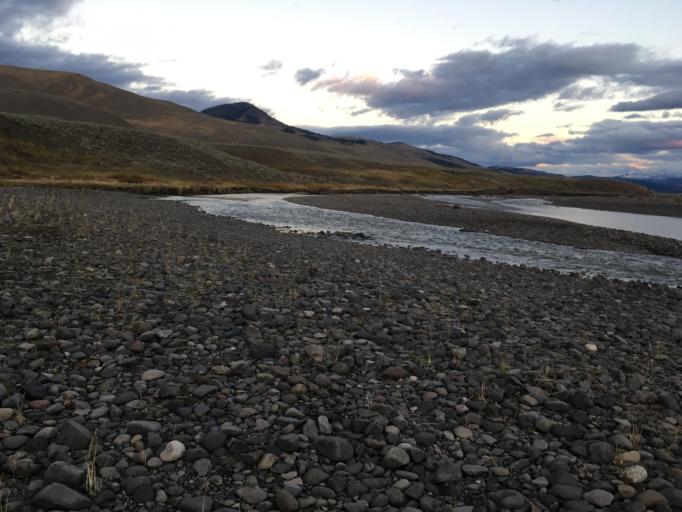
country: US
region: Montana
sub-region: Park County
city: Livingston
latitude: 44.9128
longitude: -110.2693
